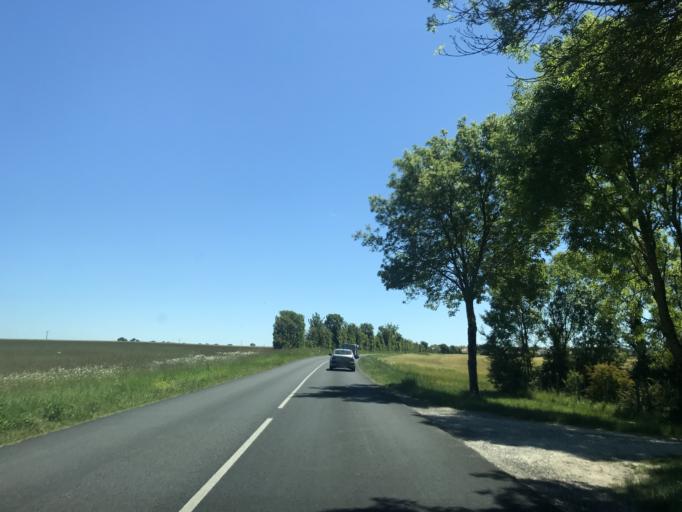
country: FR
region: Poitou-Charentes
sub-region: Departement de la Charente-Maritime
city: Meschers-sur-Gironde
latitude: 45.5832
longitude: -0.9602
